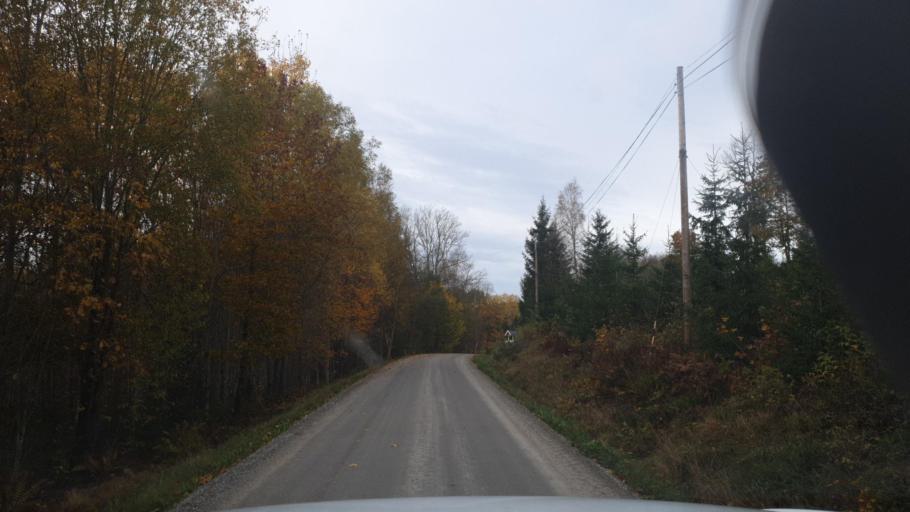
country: SE
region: Vaermland
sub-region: Sunne Kommun
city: Sunne
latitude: 59.7065
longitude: 12.8814
